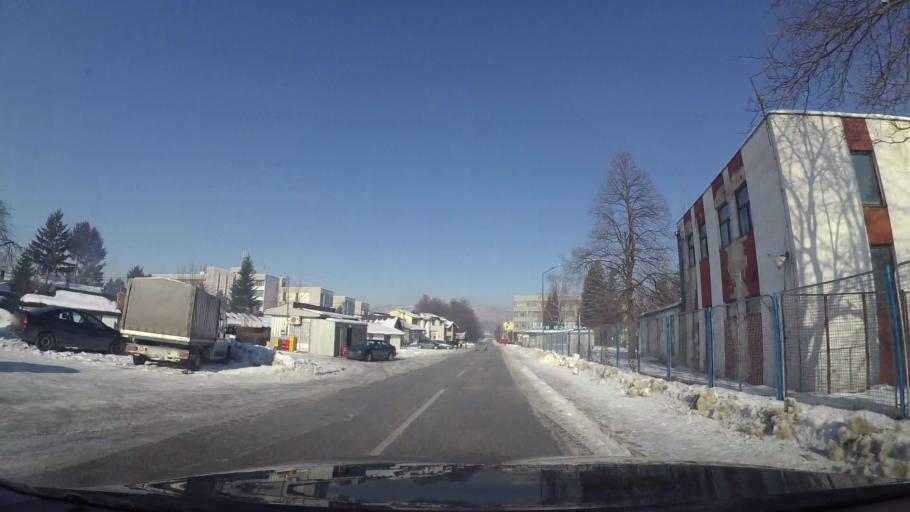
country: BA
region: Federation of Bosnia and Herzegovina
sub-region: Kanton Sarajevo
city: Sarajevo
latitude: 43.8231
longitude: 18.3766
